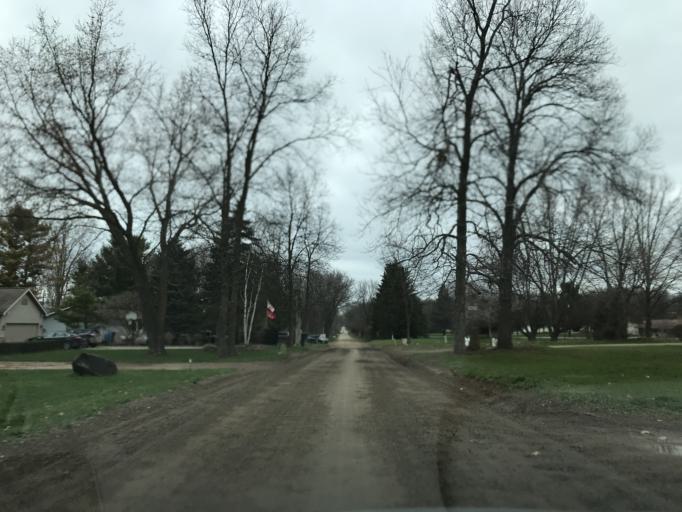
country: US
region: Michigan
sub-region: Oakland County
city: South Lyon
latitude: 42.4810
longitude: -83.6681
